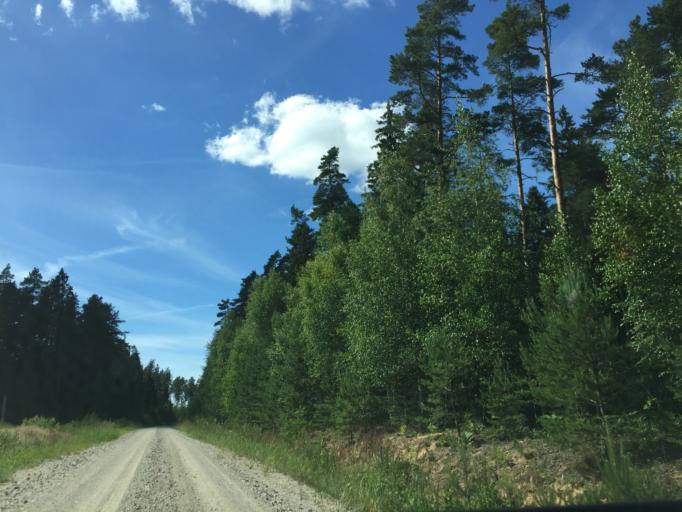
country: LV
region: Kuldigas Rajons
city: Kuldiga
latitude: 57.1015
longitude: 21.8262
